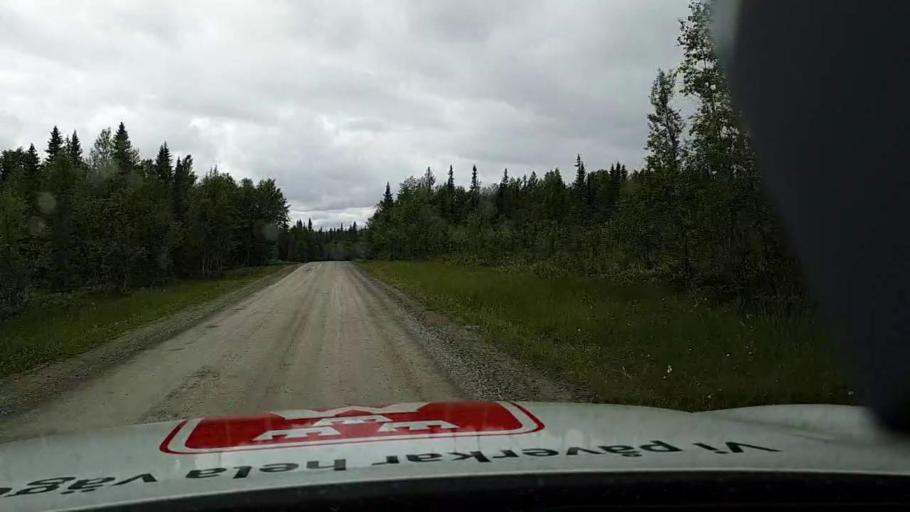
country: SE
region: Jaemtland
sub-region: Bergs Kommun
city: Hoverberg
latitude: 62.8443
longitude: 13.8405
